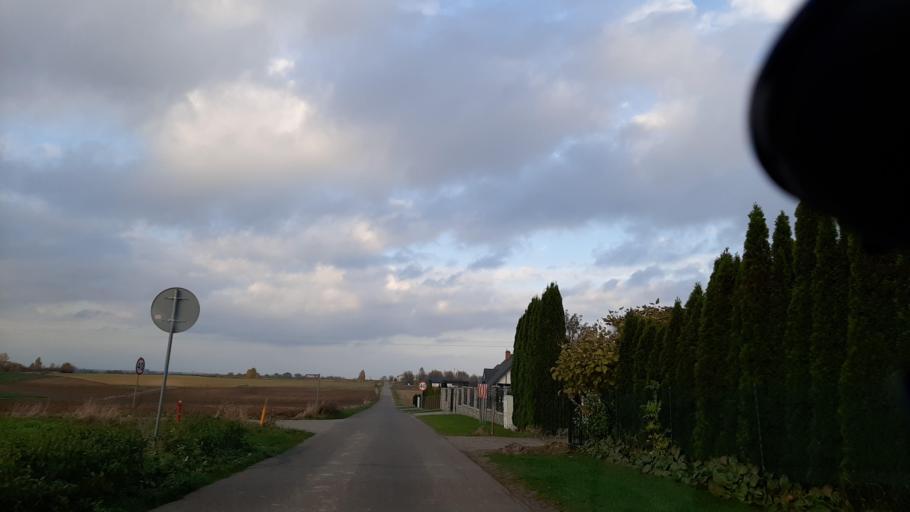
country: PL
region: Lublin Voivodeship
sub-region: Powiat lubelski
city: Garbow
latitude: 51.3411
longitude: 22.3264
